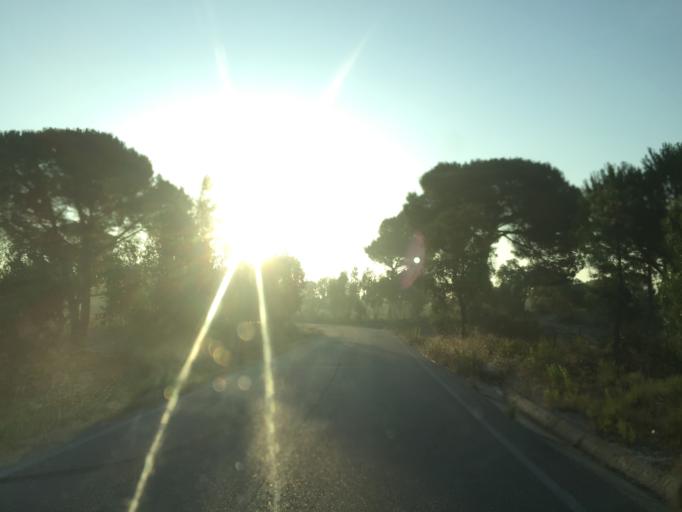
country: PT
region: Santarem
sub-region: Coruche
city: Coruche
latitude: 39.0486
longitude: -8.4309
